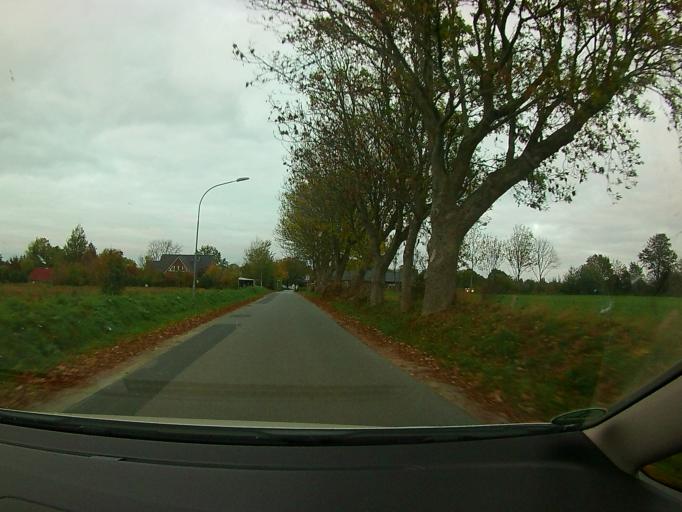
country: DE
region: Schleswig-Holstein
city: Breklum
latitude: 54.6104
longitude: 8.9880
